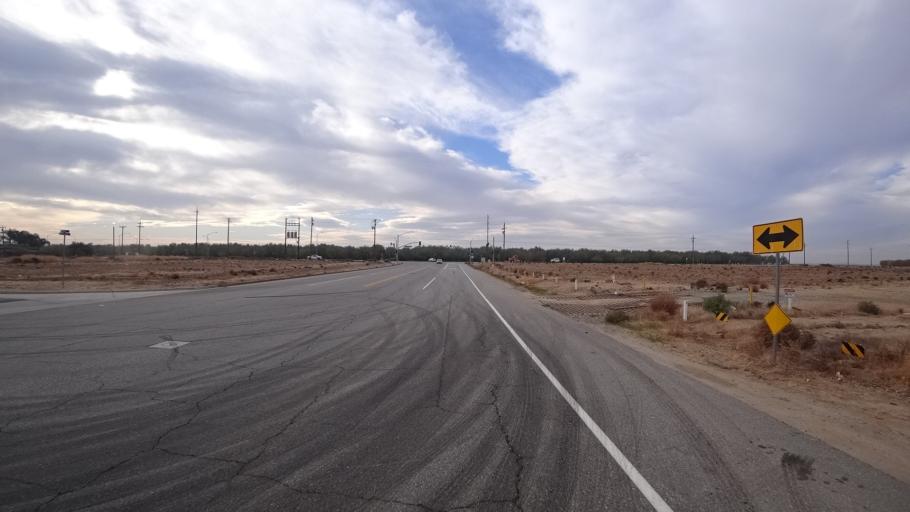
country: US
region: California
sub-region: Kern County
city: Rosedale
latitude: 35.4428
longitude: -119.2047
